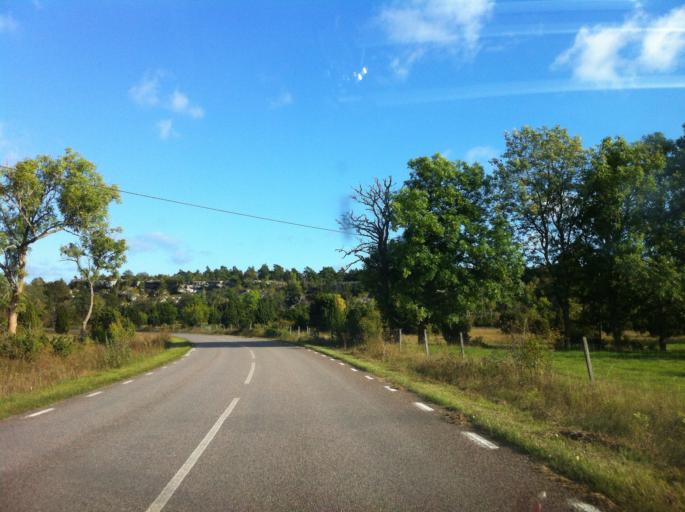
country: SE
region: Gotland
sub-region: Gotland
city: Slite
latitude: 57.4219
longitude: 18.8514
